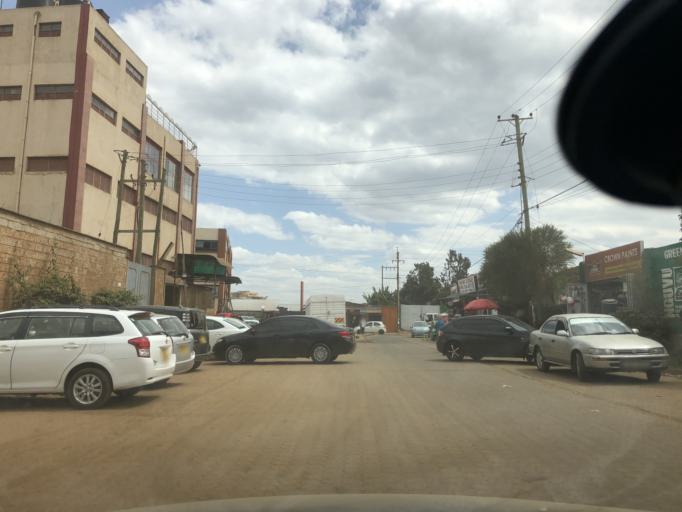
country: KE
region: Nairobi Area
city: Pumwani
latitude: -1.2321
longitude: 36.8736
